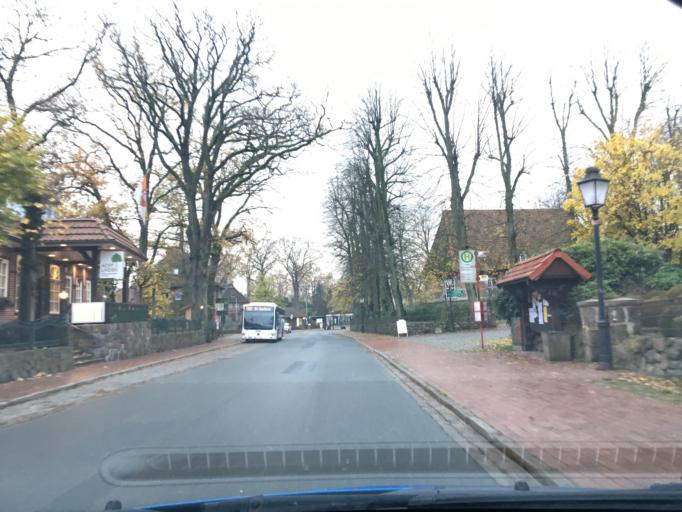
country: DE
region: Lower Saxony
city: Egestorf
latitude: 53.1943
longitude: 10.0632
